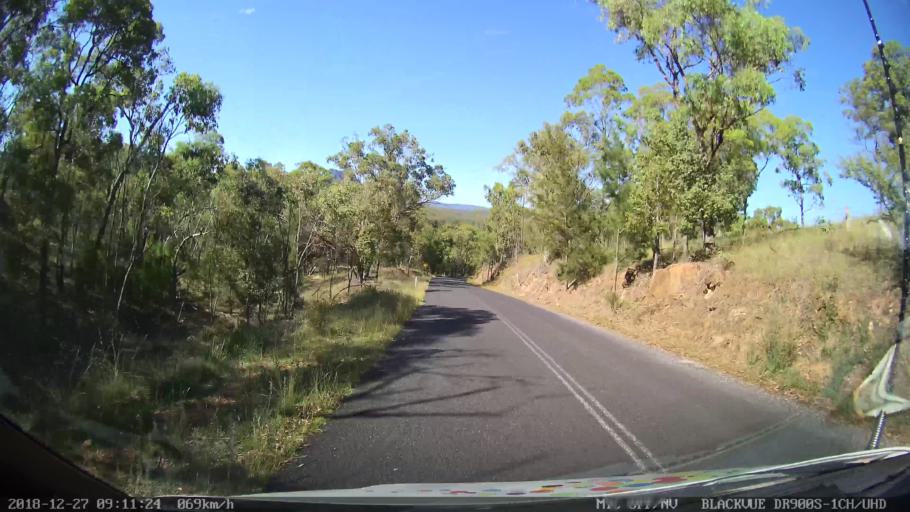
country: AU
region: New South Wales
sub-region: Lithgow
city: Portland
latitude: -33.1353
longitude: 150.1144
